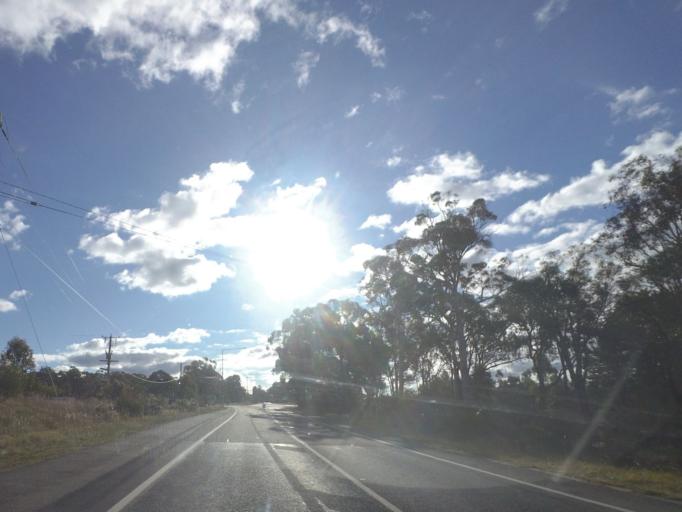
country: AU
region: Victoria
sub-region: Mount Alexander
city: Castlemaine
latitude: -37.0971
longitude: 144.3277
